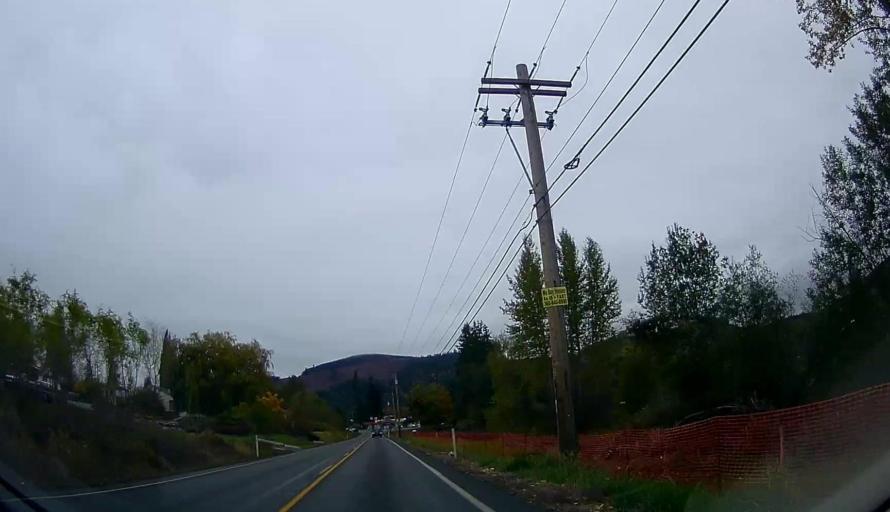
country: US
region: Washington
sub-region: Skagit County
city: Clear Lake
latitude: 48.4547
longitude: -122.2369
